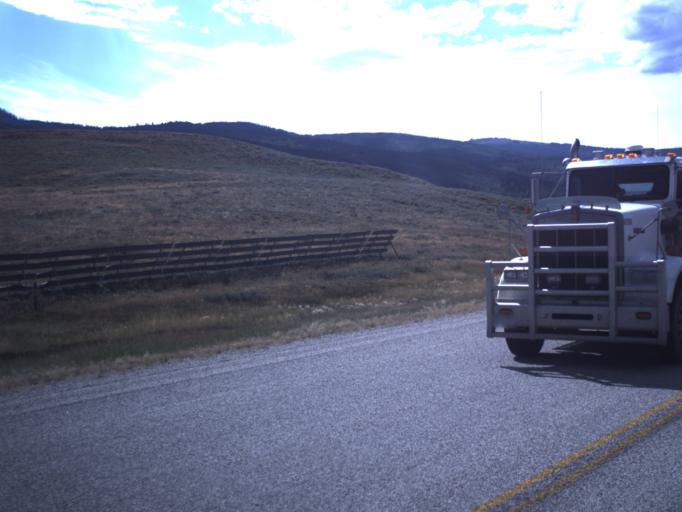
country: US
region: Utah
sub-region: Wasatch County
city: Heber
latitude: 40.2780
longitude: -111.2174
